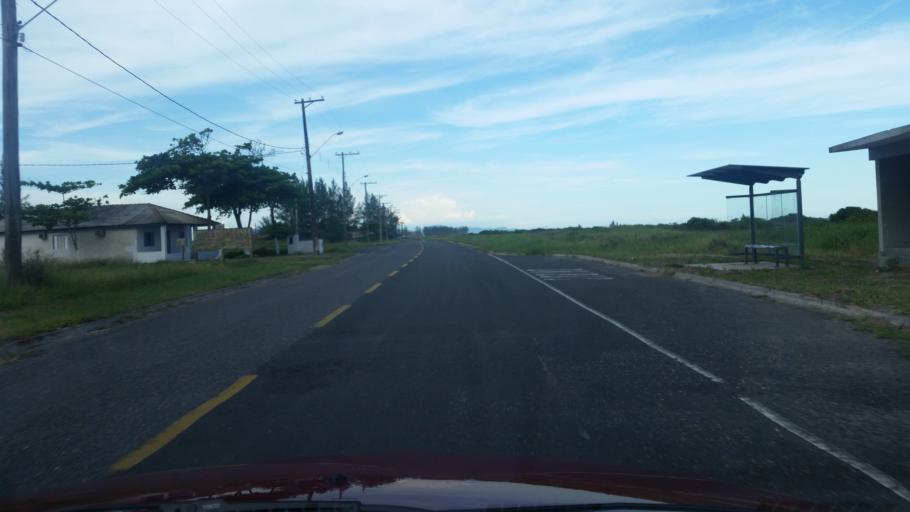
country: BR
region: Sao Paulo
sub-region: Iguape
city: Iguape
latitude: -24.8087
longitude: -47.6399
